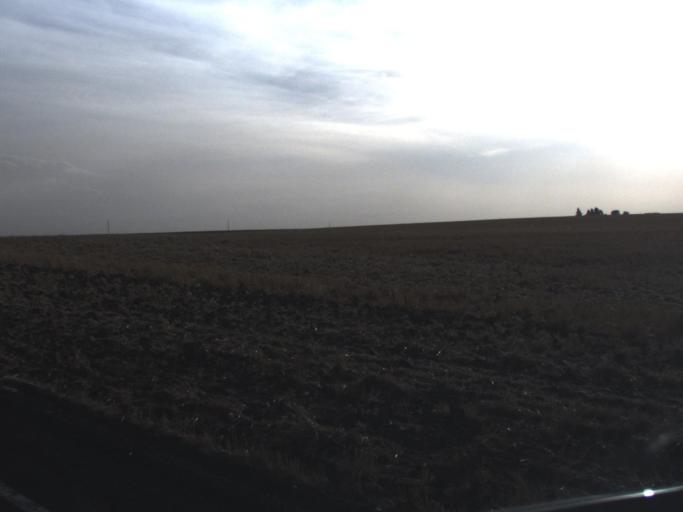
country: US
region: Washington
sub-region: Adams County
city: Ritzville
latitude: 47.2819
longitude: -118.6906
